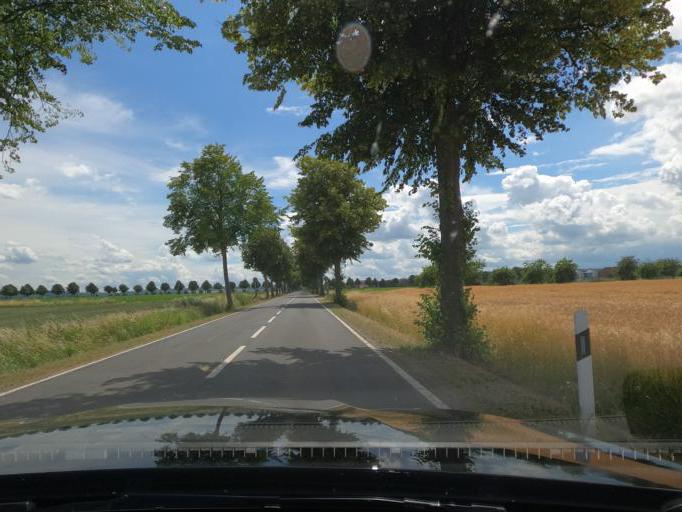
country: DE
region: Lower Saxony
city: Schellerten
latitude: 52.1781
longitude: 10.0418
